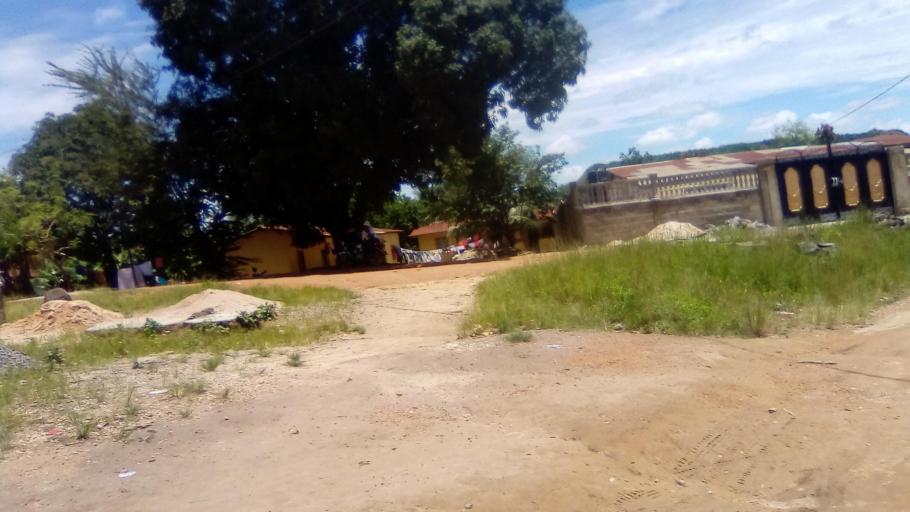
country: SL
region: Eastern Province
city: Koidu
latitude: 8.6322
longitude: -10.9887
